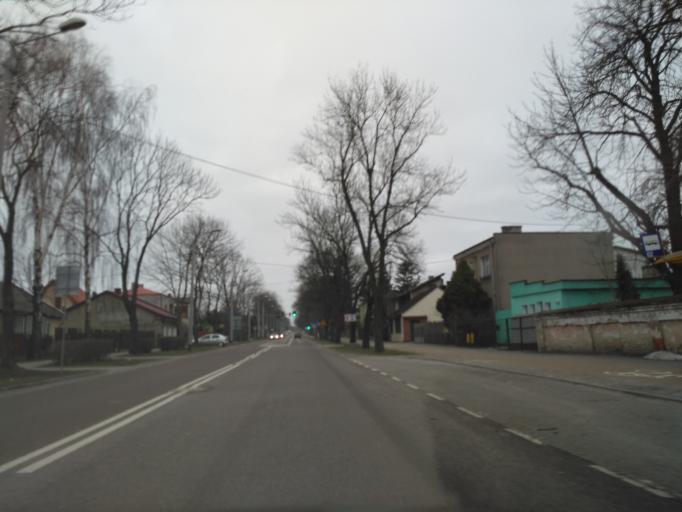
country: PL
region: Lublin Voivodeship
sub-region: Chelm
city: Chelm
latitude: 51.1277
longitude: 23.4879
